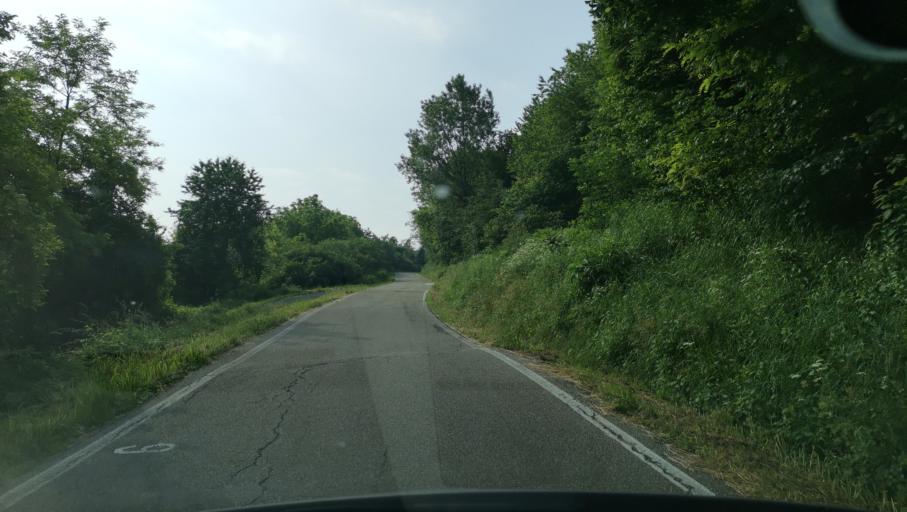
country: IT
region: Piedmont
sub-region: Provincia di Asti
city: Moncalvo
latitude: 45.0572
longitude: 8.2499
